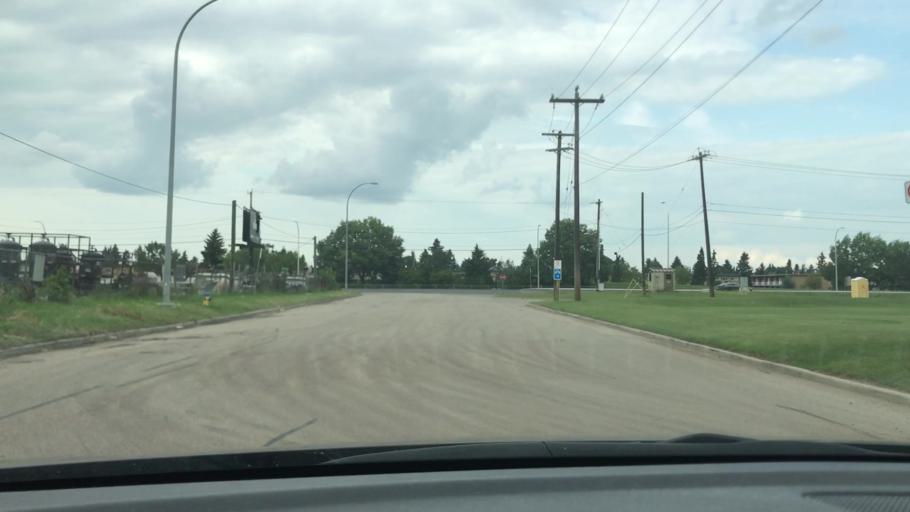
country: CA
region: Alberta
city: Edmonton
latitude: 53.5401
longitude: -113.4149
